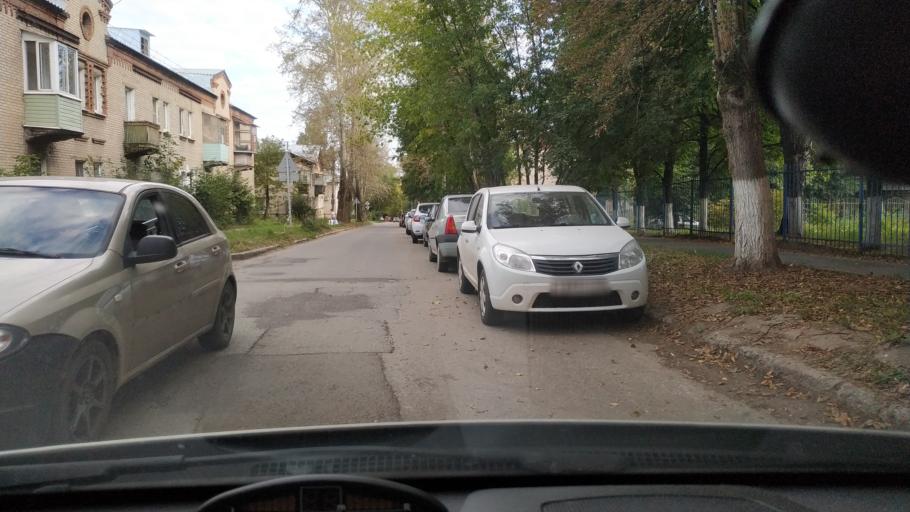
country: RU
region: Rjazan
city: Ryazan'
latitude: 54.6046
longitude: 39.7210
